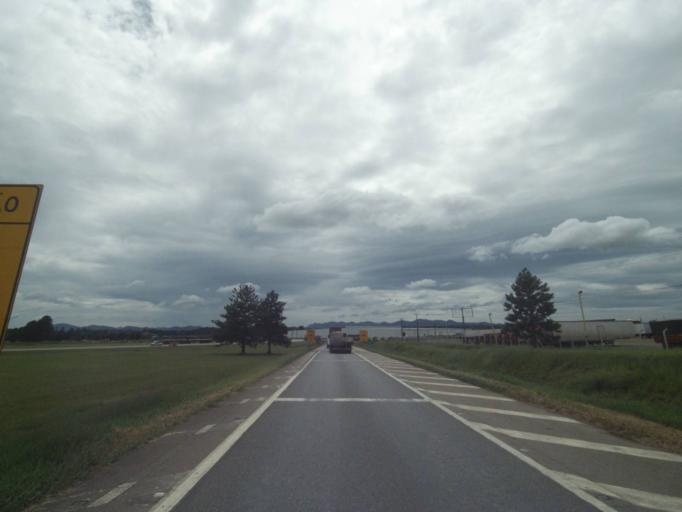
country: BR
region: Parana
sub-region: Sao Jose Dos Pinhais
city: Sao Jose dos Pinhais
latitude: -25.5135
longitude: -49.1270
